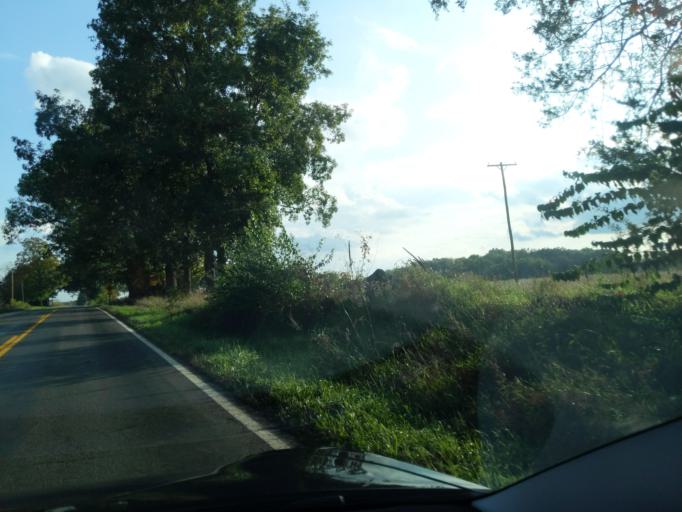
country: US
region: Michigan
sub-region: Ingham County
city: Leslie
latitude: 42.3522
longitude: -84.4629
